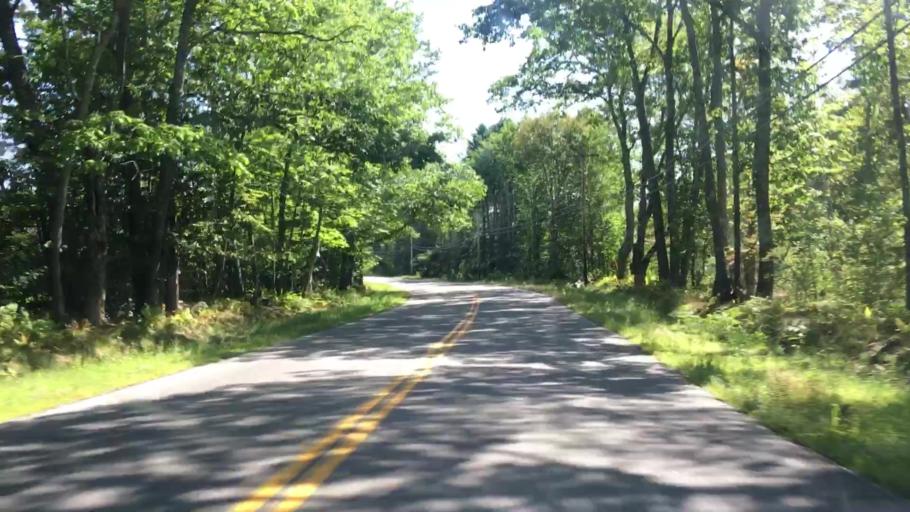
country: US
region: Maine
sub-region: Penobscot County
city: Bradford
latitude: 45.1744
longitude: -68.8527
